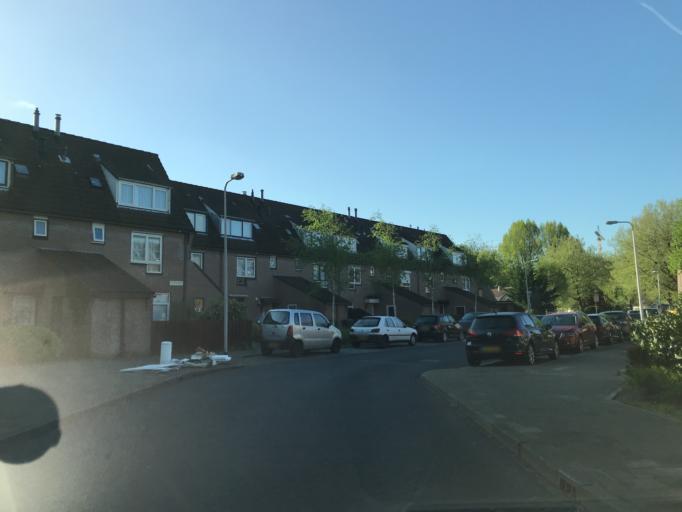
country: NL
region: North Holland
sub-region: Gemeente Diemen
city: Diemen
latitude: 52.3354
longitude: 4.9620
